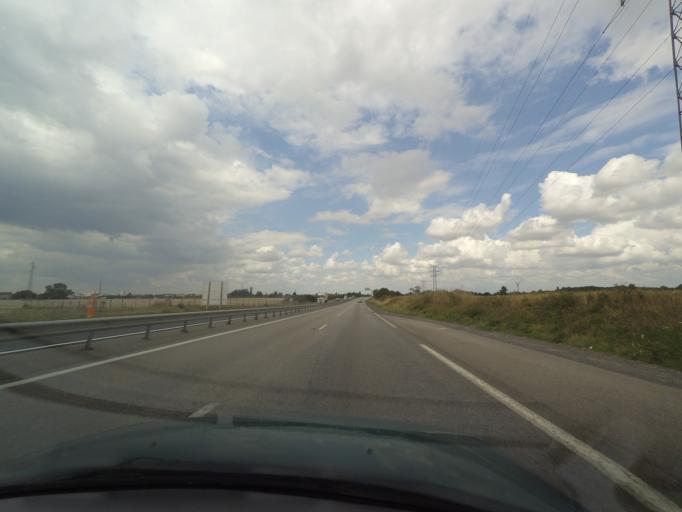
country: FR
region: Poitou-Charentes
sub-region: Departement de la Vienne
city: Mignaloux-Beauvoir
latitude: 46.5802
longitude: 0.3951
